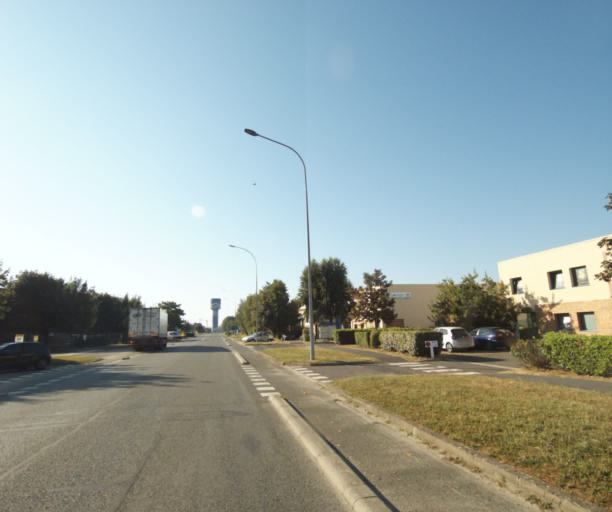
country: FR
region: Ile-de-France
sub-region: Departement de Seine-et-Marne
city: Lieusaint
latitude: 48.6228
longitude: 2.5664
